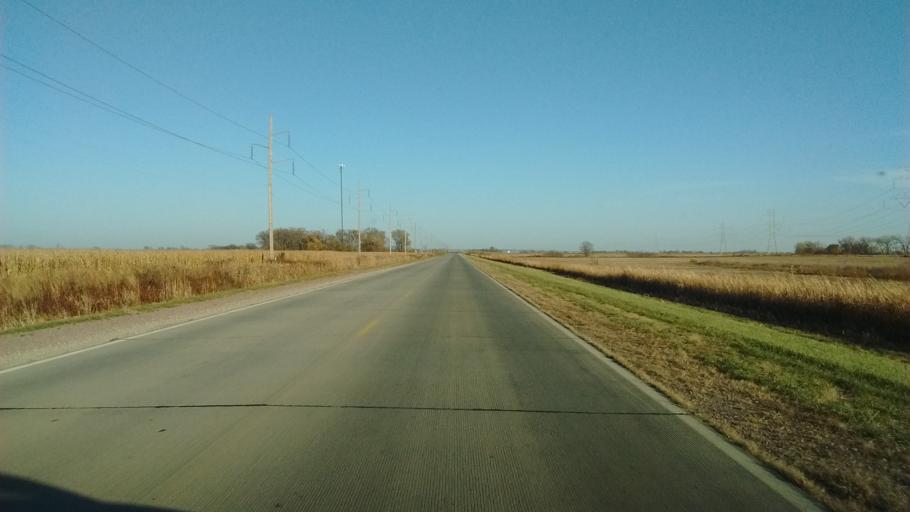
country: US
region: Iowa
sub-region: Woodbury County
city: Sergeant Bluff
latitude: 42.3302
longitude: -96.3442
